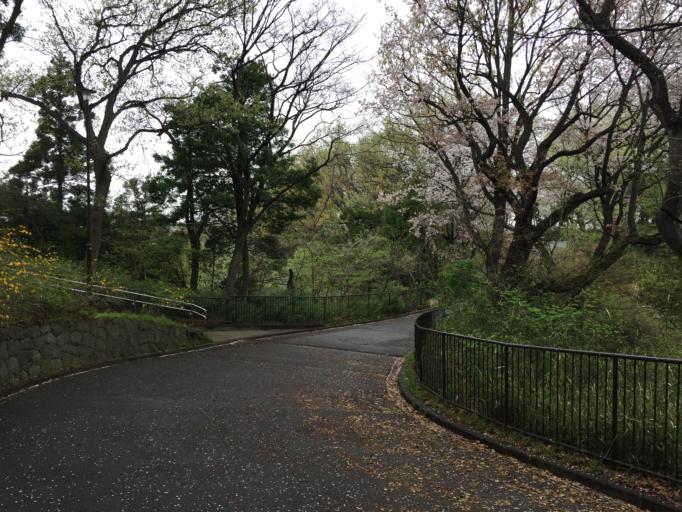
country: JP
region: Kanagawa
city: Yokohama
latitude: 35.4237
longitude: 139.5956
